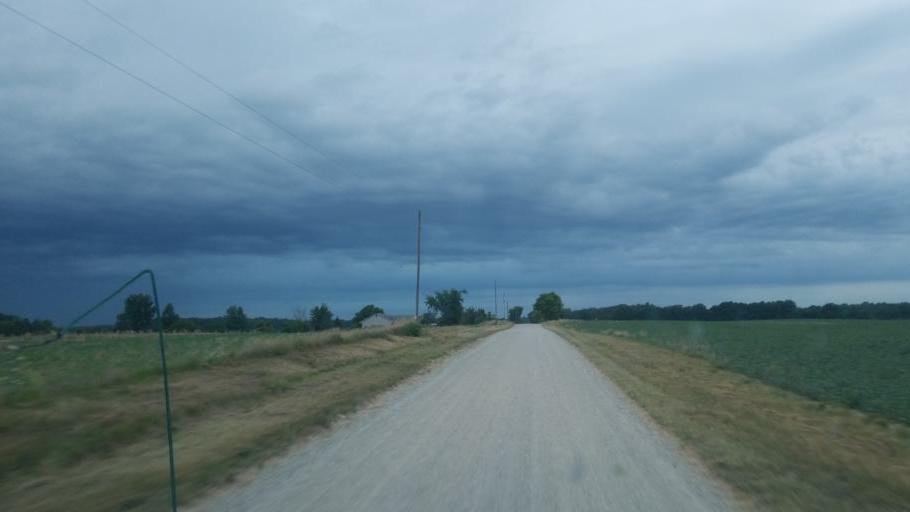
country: US
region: Ohio
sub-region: Defiance County
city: Hicksville
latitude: 41.3286
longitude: -84.8319
